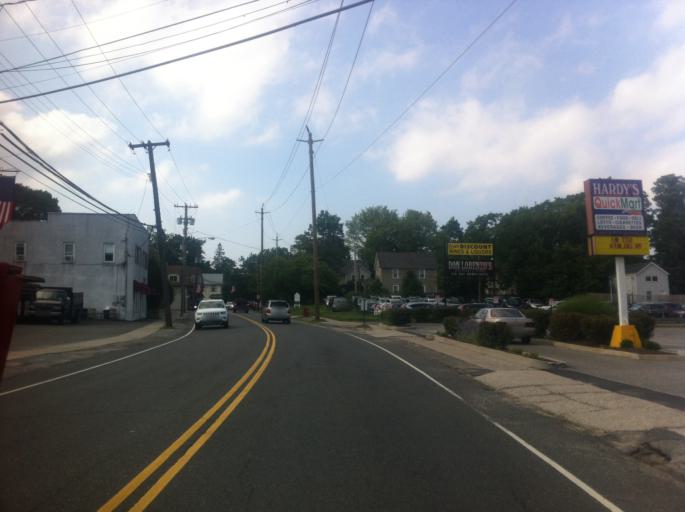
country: US
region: New York
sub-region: Nassau County
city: Glen Head
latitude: 40.8348
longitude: -73.6300
